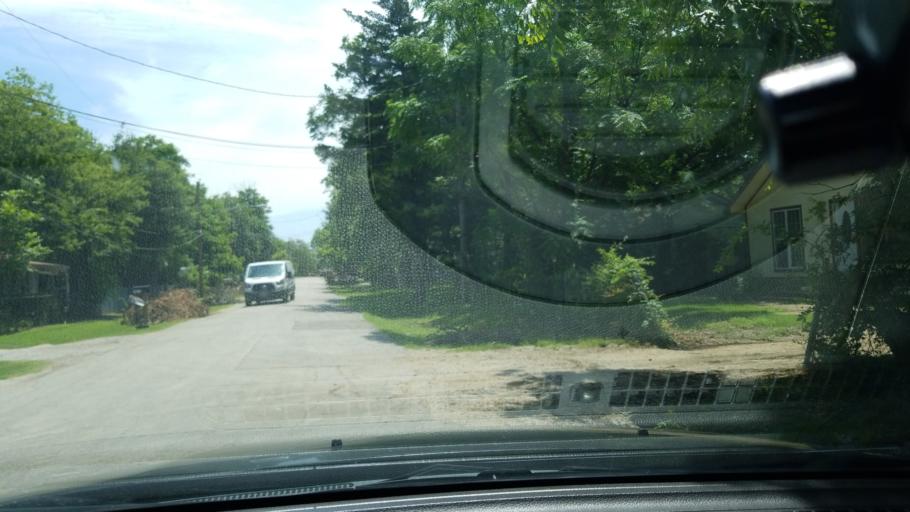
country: US
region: Texas
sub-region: Dallas County
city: Balch Springs
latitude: 32.7462
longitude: -96.6421
